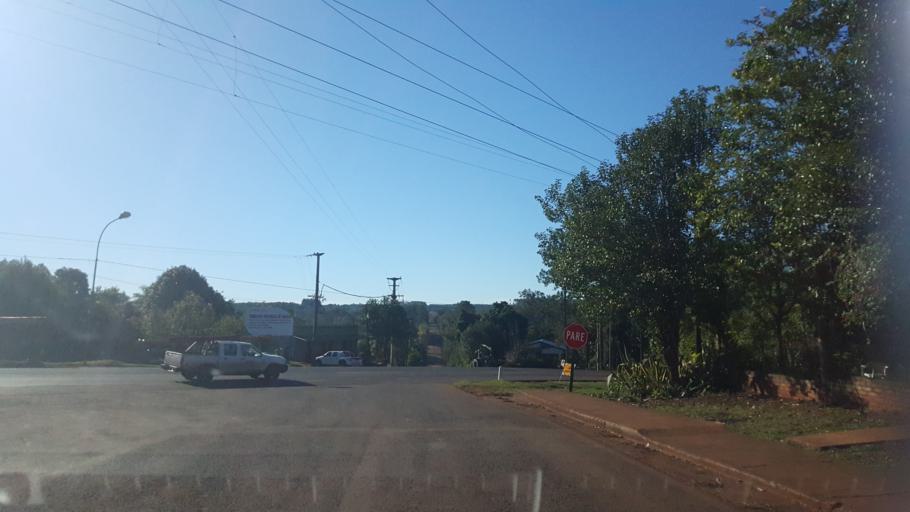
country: AR
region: Misiones
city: Jardin America
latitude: -27.0839
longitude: -55.2865
